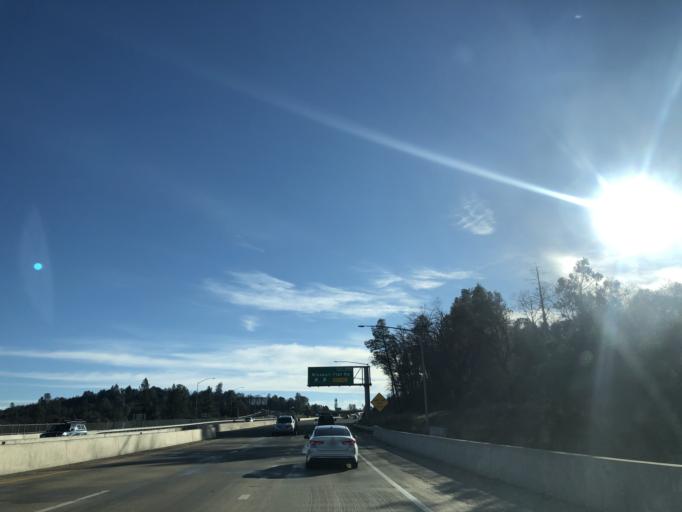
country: US
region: California
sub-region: El Dorado County
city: Diamond Springs
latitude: 38.7166
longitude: -120.8373
